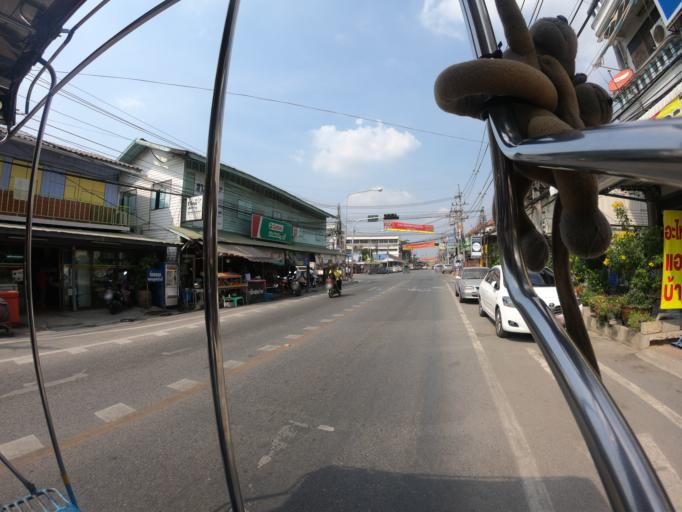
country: TH
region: Phra Nakhon Si Ayutthaya
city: Phra Nakhon Si Ayutthaya
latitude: 14.3543
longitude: 100.5804
